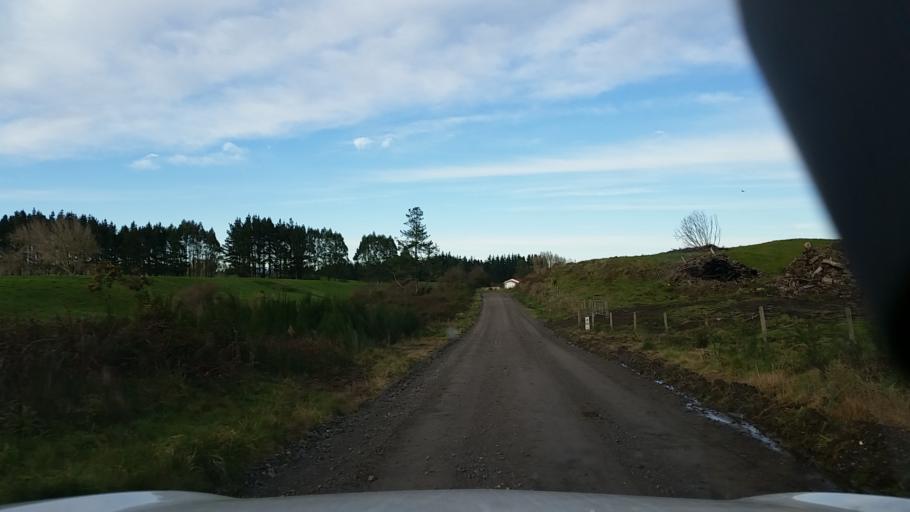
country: NZ
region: Bay of Plenty
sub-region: Rotorua District
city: Rotorua
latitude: -38.2624
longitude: 176.1597
